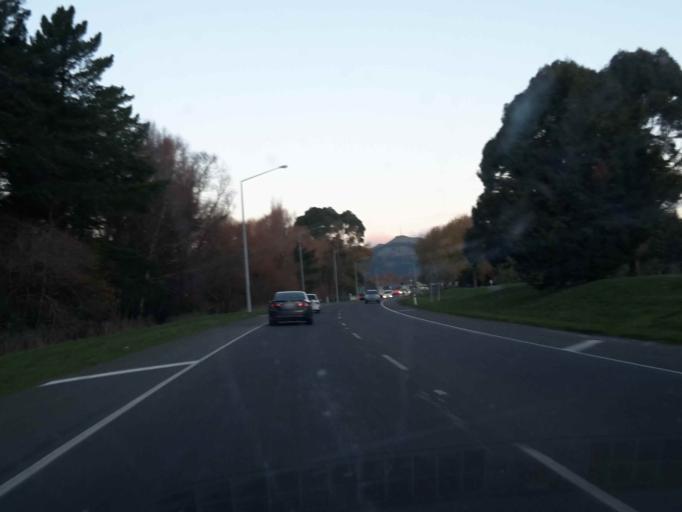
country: NZ
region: Canterbury
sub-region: Christchurch City
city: Christchurch
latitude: -43.5515
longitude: 172.5886
